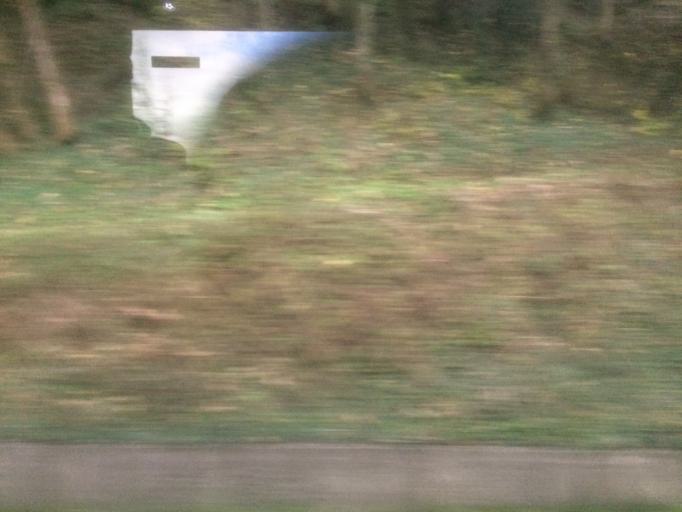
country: GB
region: Scotland
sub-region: Stirling
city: Stirling
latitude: 56.1260
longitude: -3.9502
